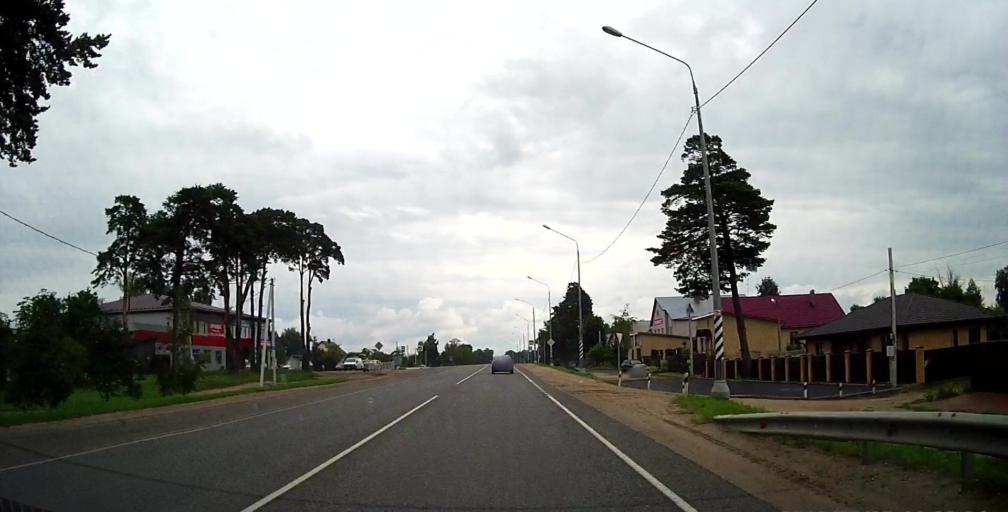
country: RU
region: Smolensk
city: Katyn'
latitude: 54.7842
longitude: 31.8450
